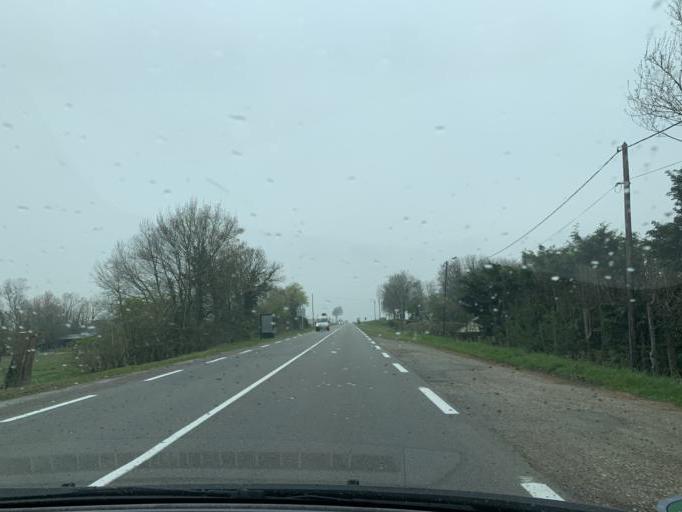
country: FR
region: Picardie
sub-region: Departement de la Somme
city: Nouvion
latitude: 50.1896
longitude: 1.7939
